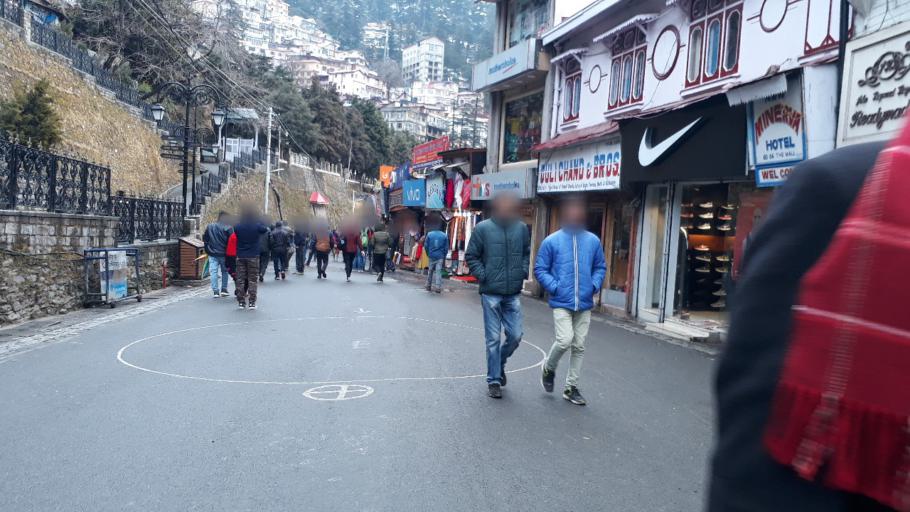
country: IN
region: Himachal Pradesh
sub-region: Shimla
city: Shimla
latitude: 31.1039
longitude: 77.1760
